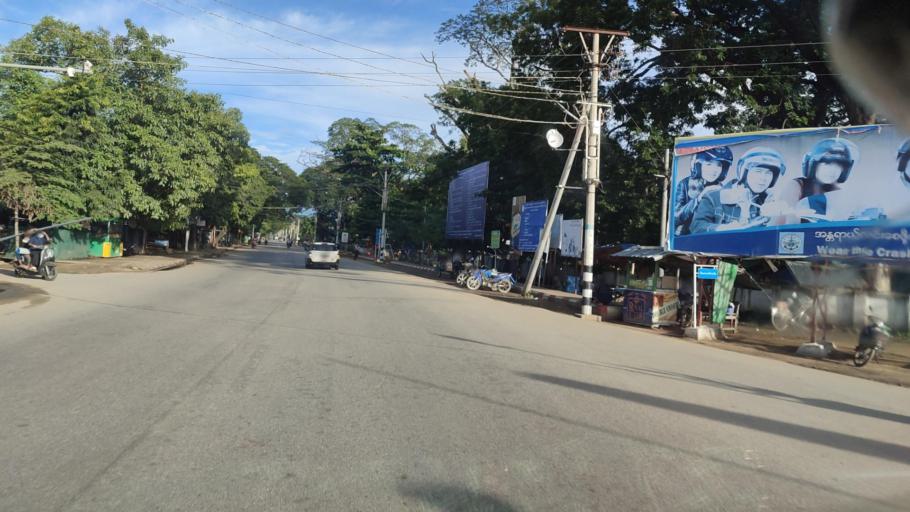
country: MM
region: Mandalay
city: Yamethin
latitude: 20.1291
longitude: 96.2020
